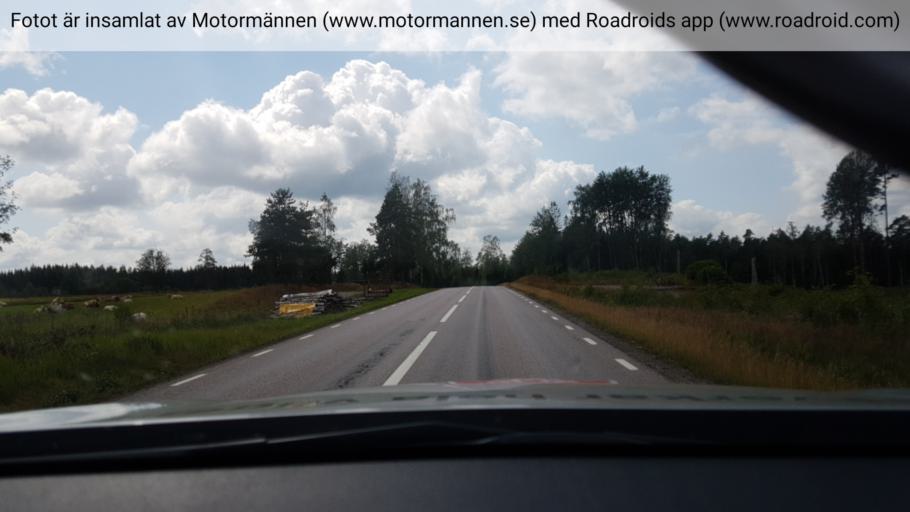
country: SE
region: Vaestra Goetaland
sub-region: Svenljunga Kommun
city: Svenljunga
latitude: 57.4819
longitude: 13.0435
